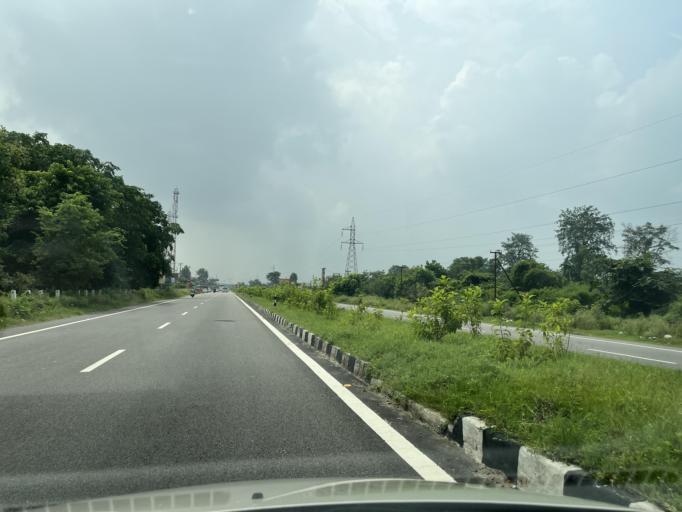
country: IN
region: Uttarakhand
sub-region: Dehradun
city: Raiwala
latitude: 30.0903
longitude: 78.1851
